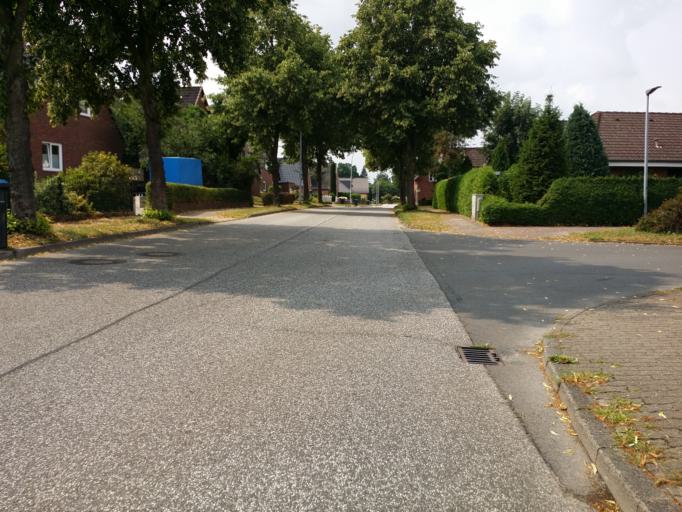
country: DE
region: Schleswig-Holstein
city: Heiligenstedtenerkamp
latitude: 53.9039
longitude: 9.4763
